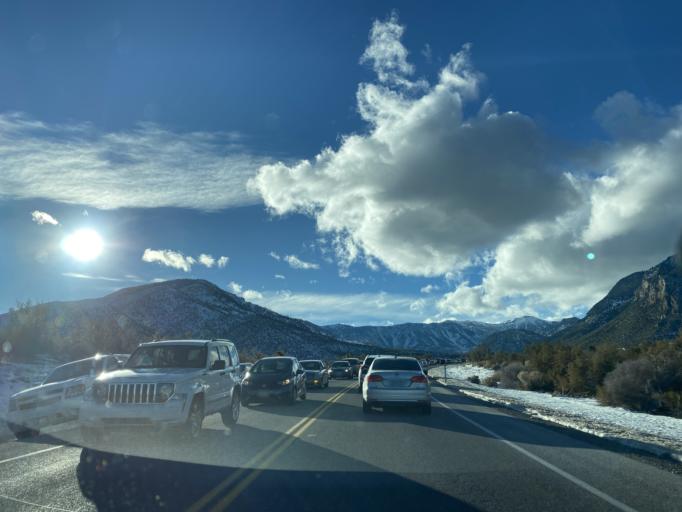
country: US
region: Nevada
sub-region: Clark County
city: Summerlin South
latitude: 36.2699
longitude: -115.5606
